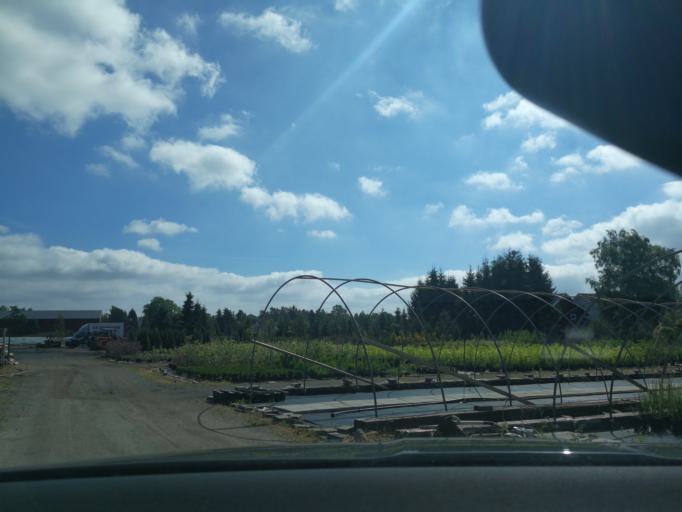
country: NO
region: Vestfold
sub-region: Sandefjord
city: Sandefjord
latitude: 59.1524
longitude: 10.1976
